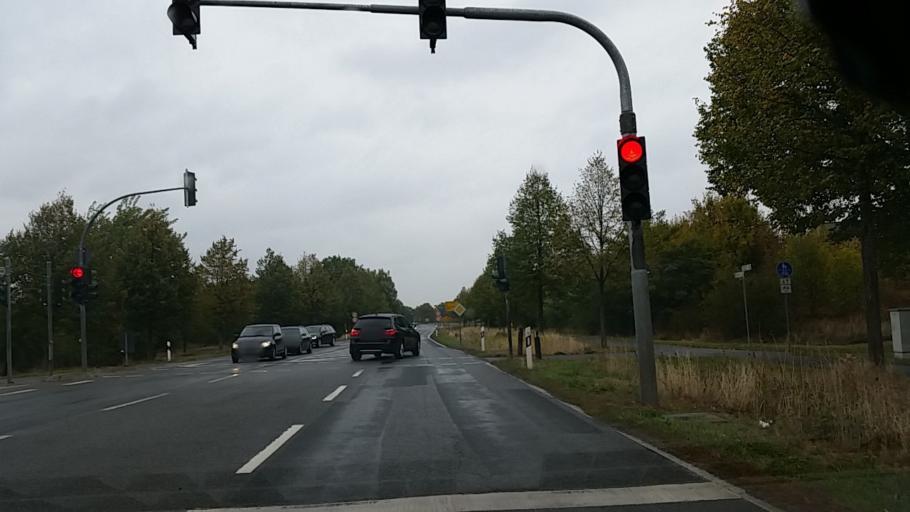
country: DE
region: Lower Saxony
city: Wolfsburg
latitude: 52.4488
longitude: 10.8279
